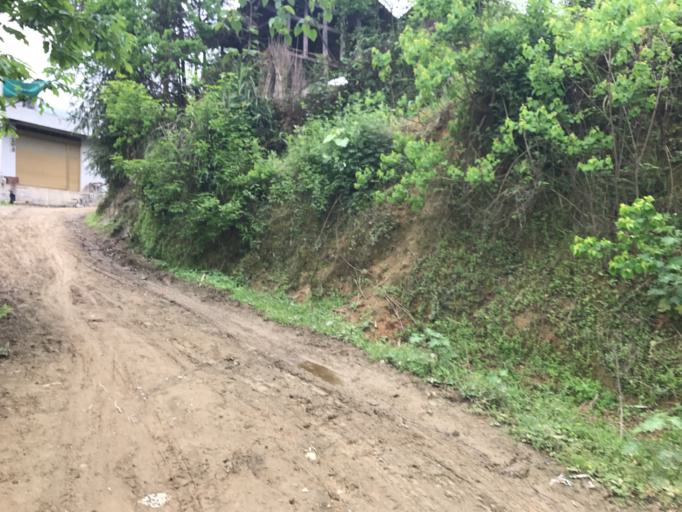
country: CN
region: Guizhou Sheng
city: Xujiaba
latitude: 27.7283
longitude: 108.0121
